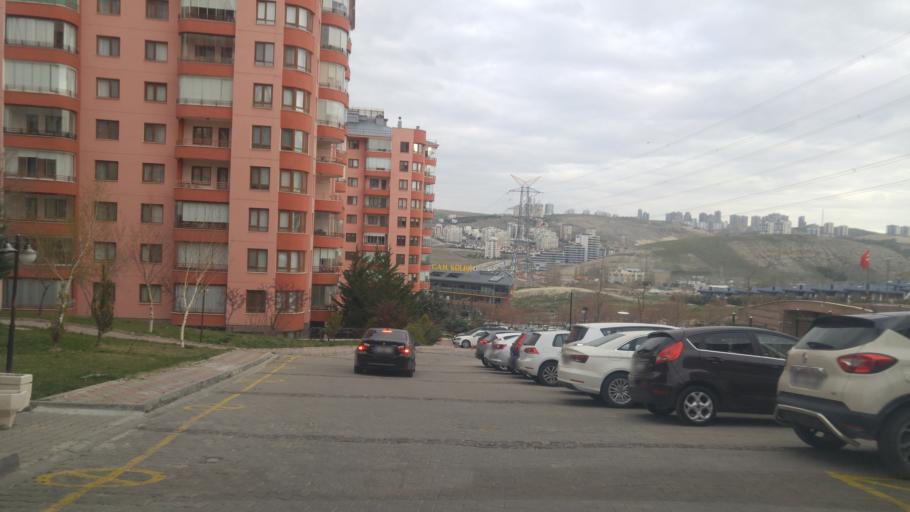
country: TR
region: Ankara
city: Etimesgut
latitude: 39.8609
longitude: 32.6730
